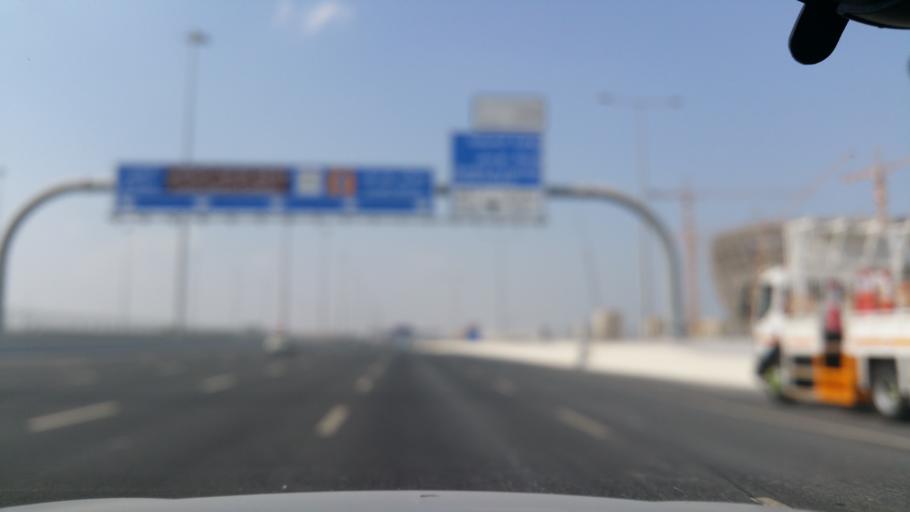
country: QA
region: Baladiyat Umm Salal
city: Umm Salal Muhammad
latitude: 25.4159
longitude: 51.4880
